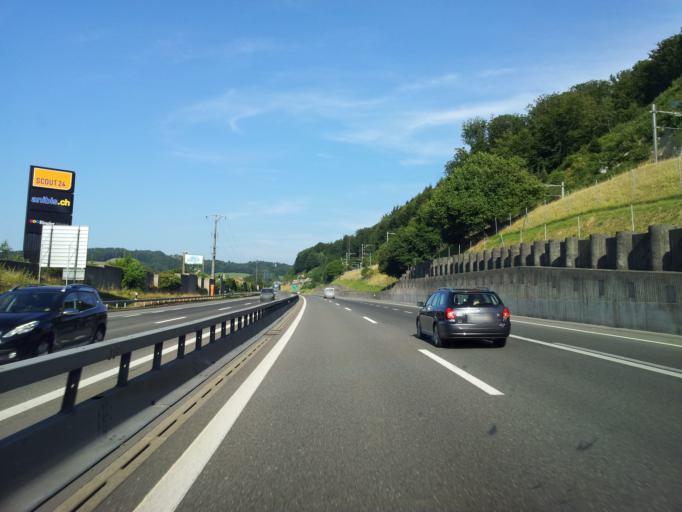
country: CH
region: Fribourg
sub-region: Sense District
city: Flamatt
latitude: 46.8881
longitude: 7.3277
